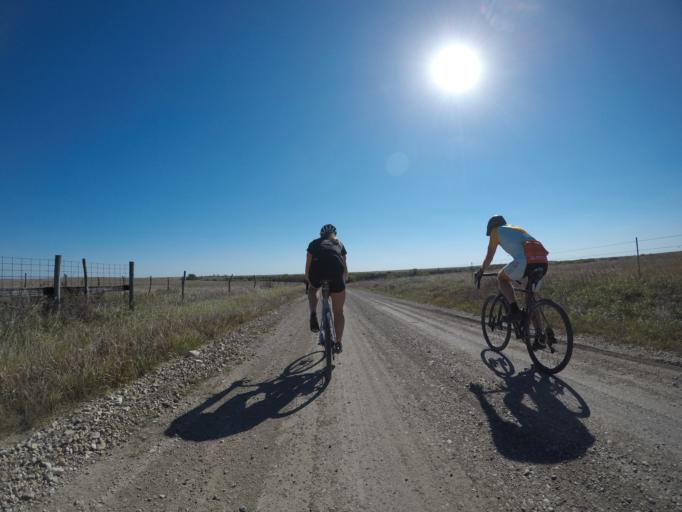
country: US
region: Kansas
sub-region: Wabaunsee County
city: Alma
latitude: 38.9519
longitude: -96.4641
